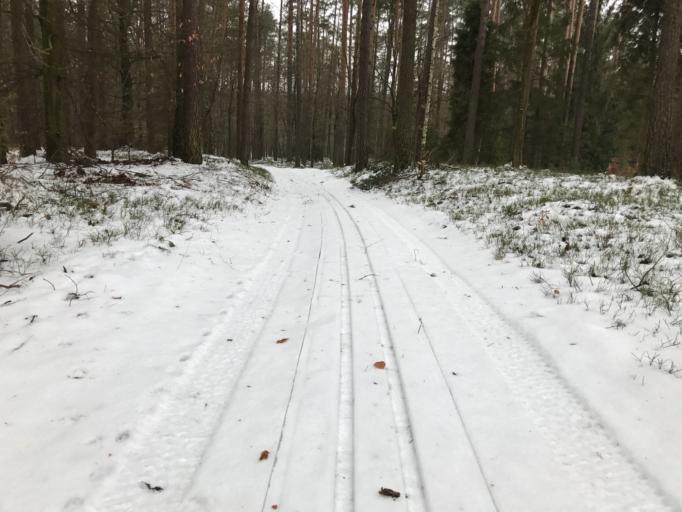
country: PL
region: Kujawsko-Pomorskie
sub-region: Powiat brodnicki
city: Gorzno
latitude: 53.1876
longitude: 19.6930
